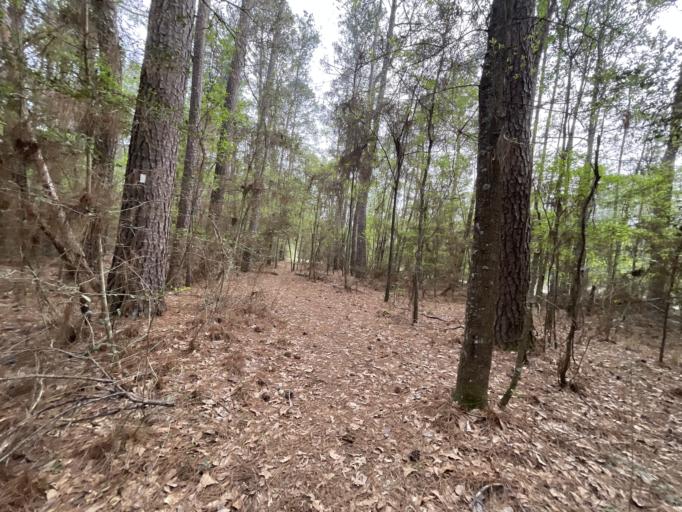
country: US
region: Texas
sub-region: Walker County
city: Huntsville
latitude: 30.6518
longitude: -95.4846
